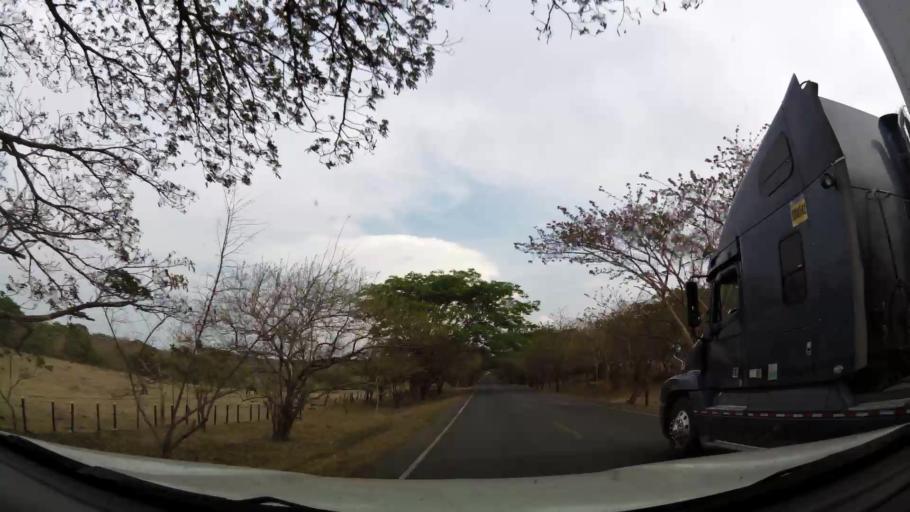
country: NI
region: Rivas
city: Cardenas
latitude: 11.2687
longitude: -85.6486
